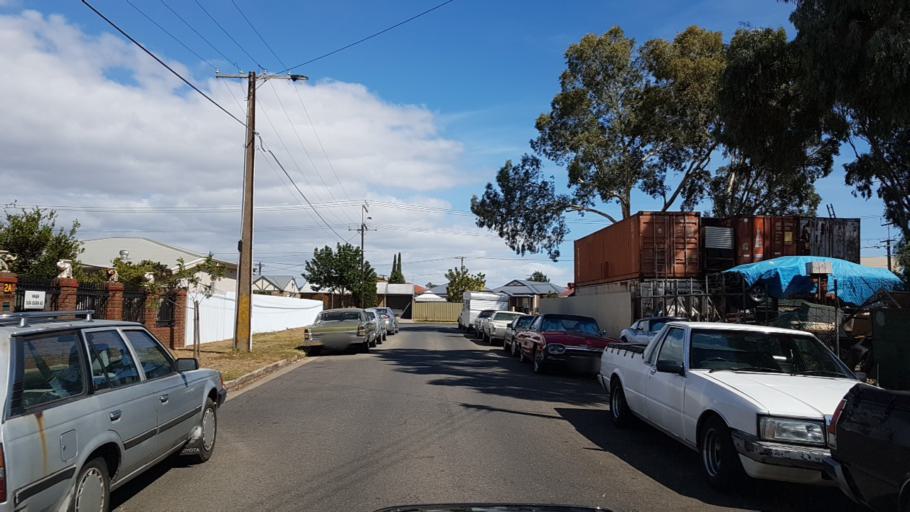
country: AU
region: South Australia
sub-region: Charles Sturt
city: Woodville North
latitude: -34.8551
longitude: 138.5427
